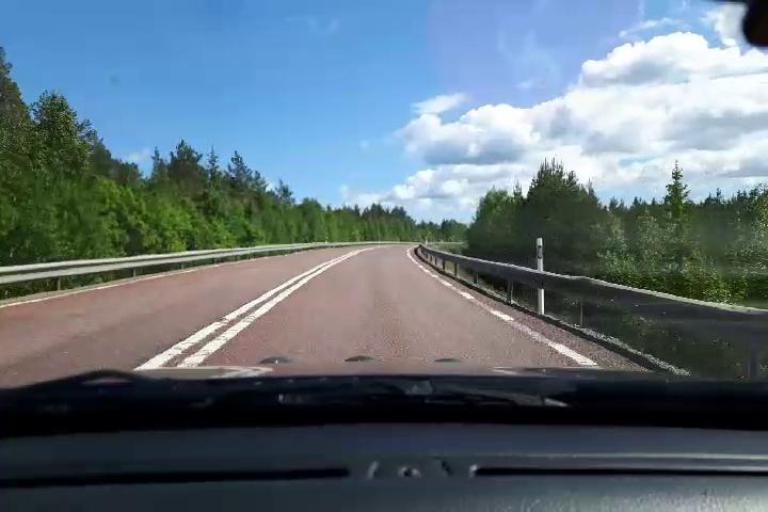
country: SE
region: Gaevleborg
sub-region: Hudiksvalls Kommun
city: Delsbo
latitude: 61.7863
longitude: 16.6310
